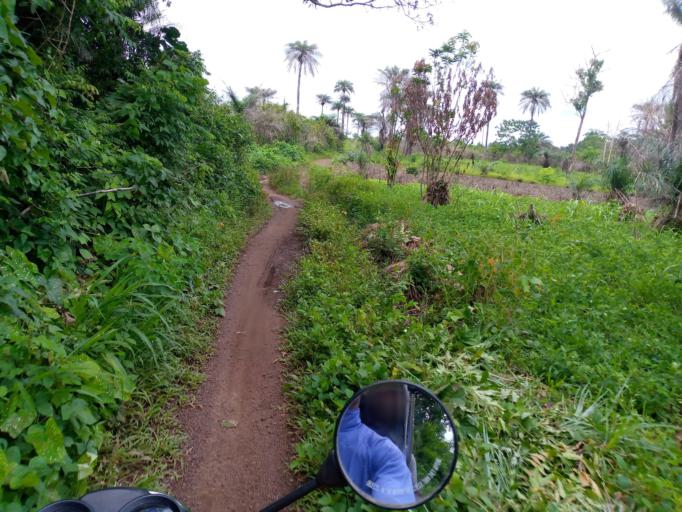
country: SL
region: Northern Province
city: Mange
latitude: 8.9914
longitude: -12.7724
